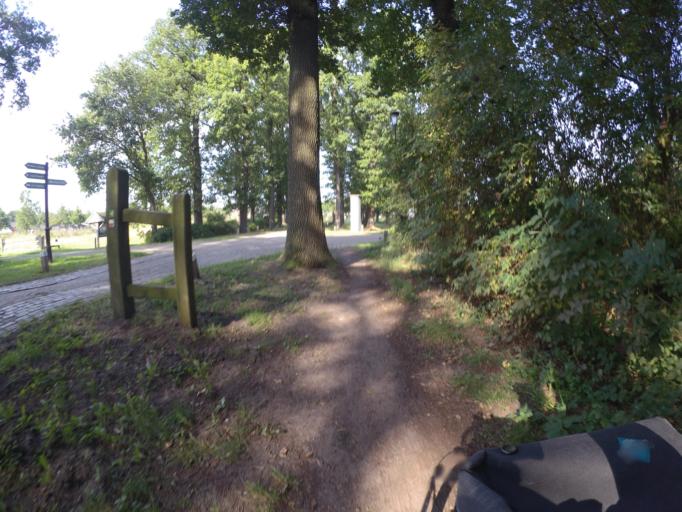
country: NL
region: North Brabant
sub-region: Gemeente Haaren
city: Haaren
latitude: 51.5936
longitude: 5.2343
